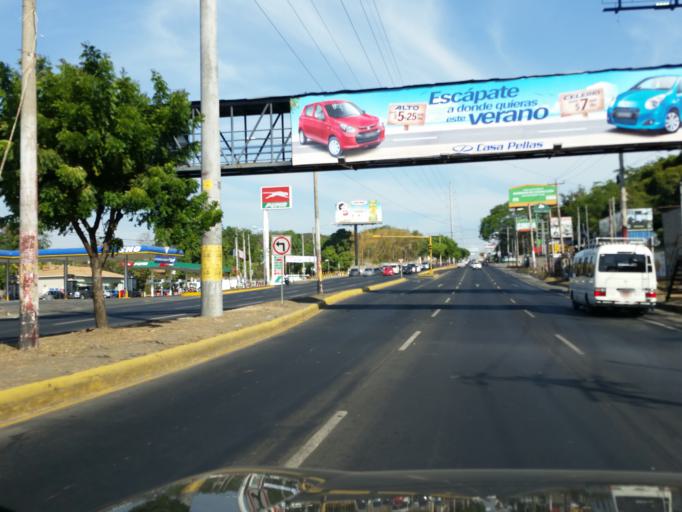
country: NI
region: Managua
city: Managua
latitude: 12.0984
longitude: -86.2419
